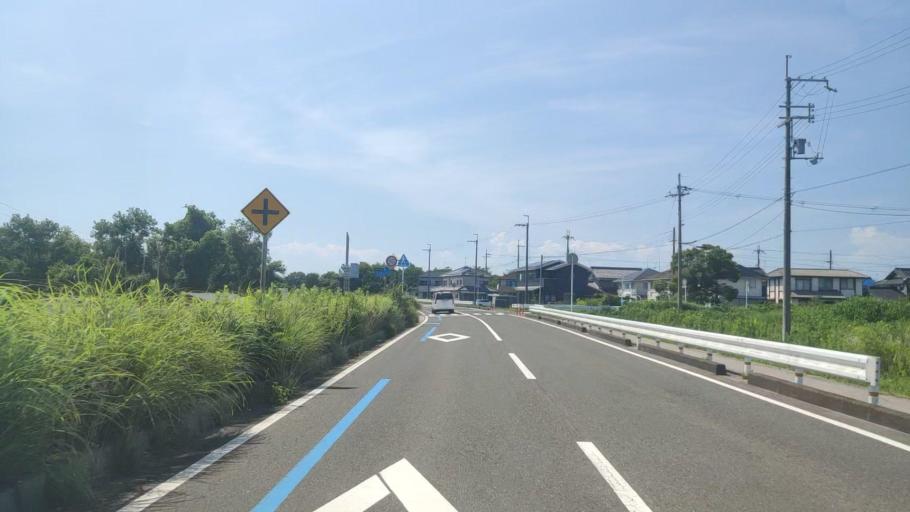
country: JP
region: Shiga Prefecture
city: Nagahama
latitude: 35.3865
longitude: 136.2454
